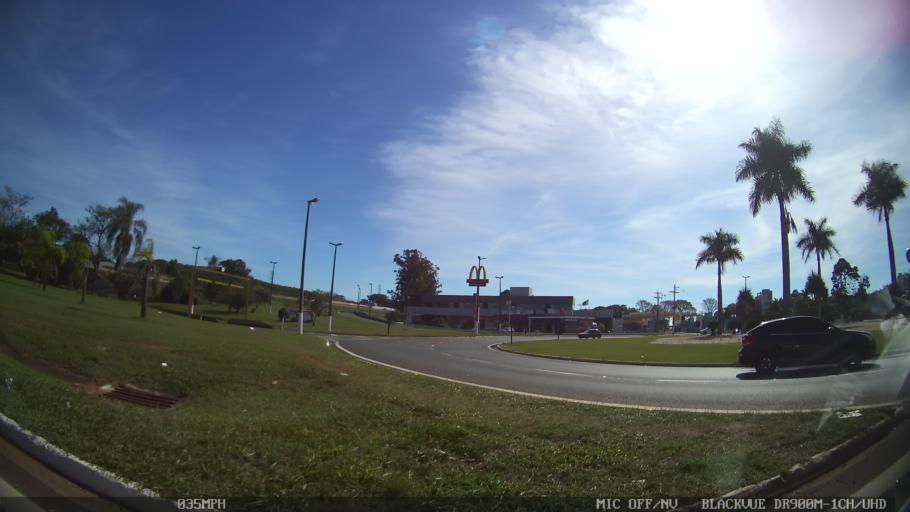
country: BR
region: Sao Paulo
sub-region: Leme
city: Leme
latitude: -22.1896
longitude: -47.3971
